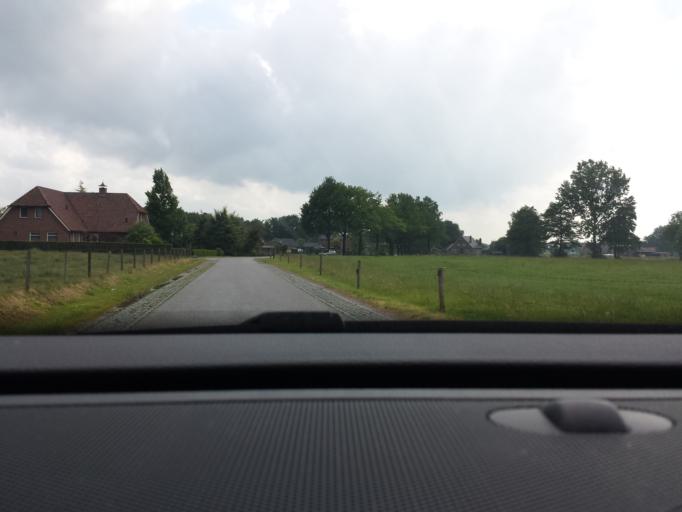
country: NL
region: Gelderland
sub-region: Berkelland
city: Eibergen
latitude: 52.0529
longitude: 6.6084
